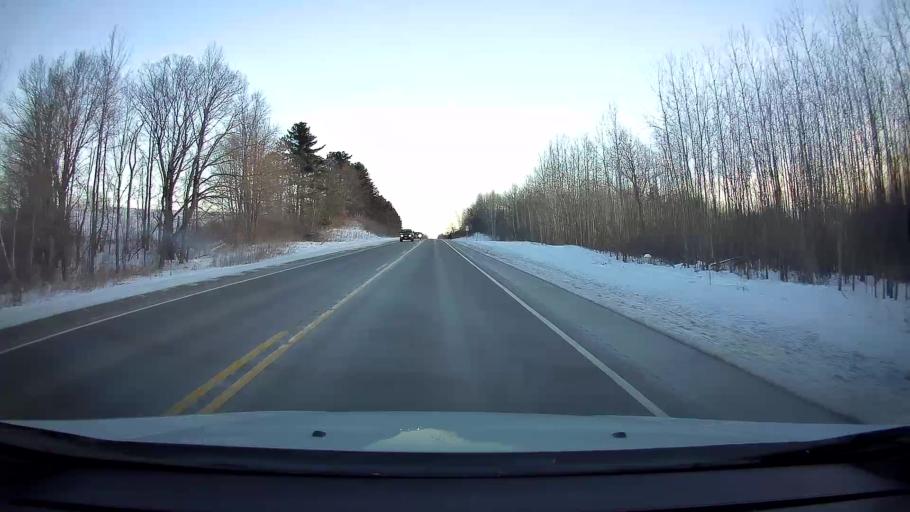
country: US
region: Wisconsin
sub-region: Washburn County
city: Shell Lake
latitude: 45.6798
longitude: -91.9859
